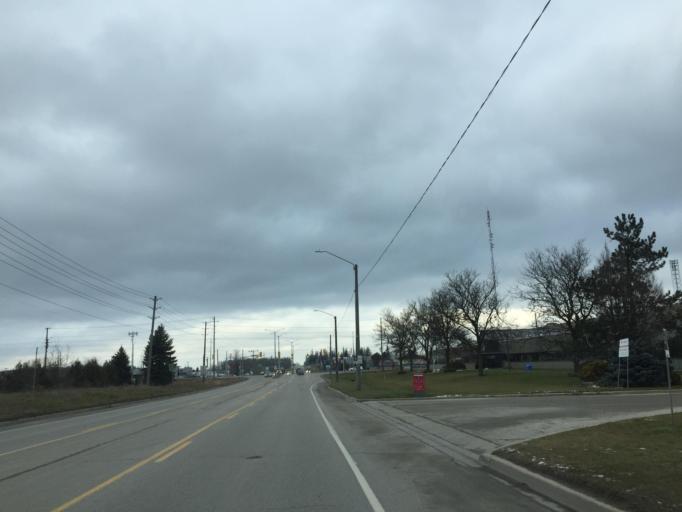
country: CA
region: Ontario
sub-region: Wellington County
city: Guelph
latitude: 43.5372
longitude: -80.3124
